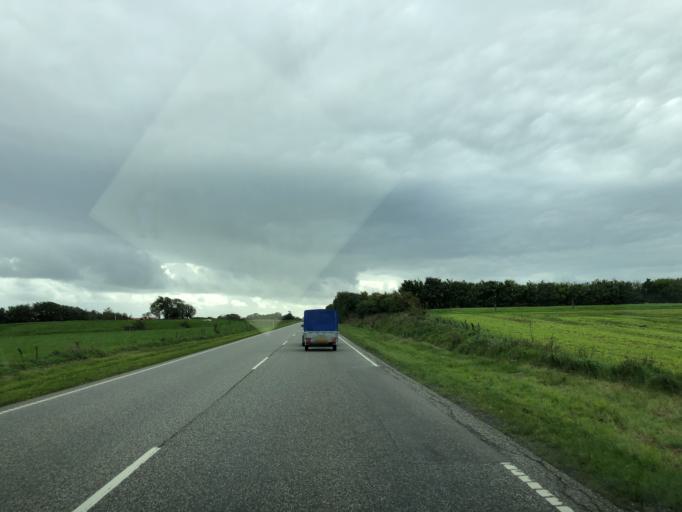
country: DK
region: North Denmark
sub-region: Thisted Kommune
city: Thisted
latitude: 56.9564
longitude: 8.6445
